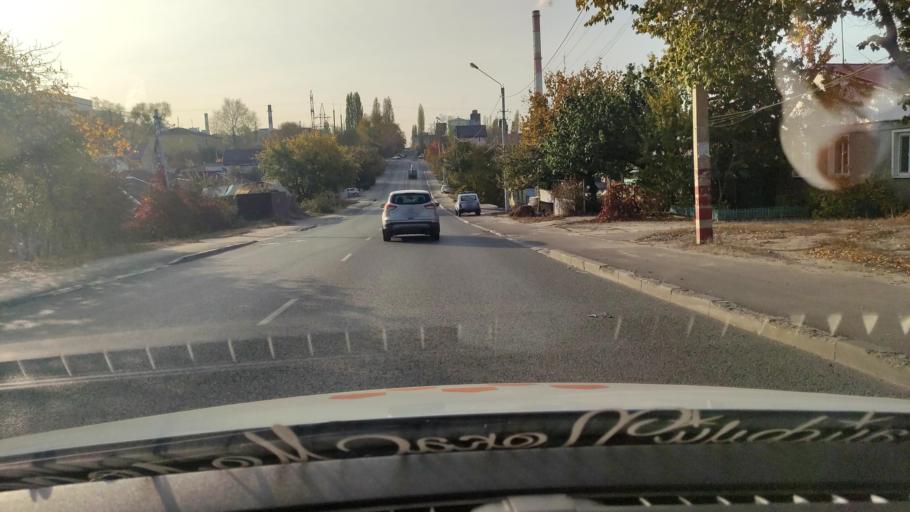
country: RU
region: Voronezj
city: Voronezh
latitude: 51.6924
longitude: 39.1576
